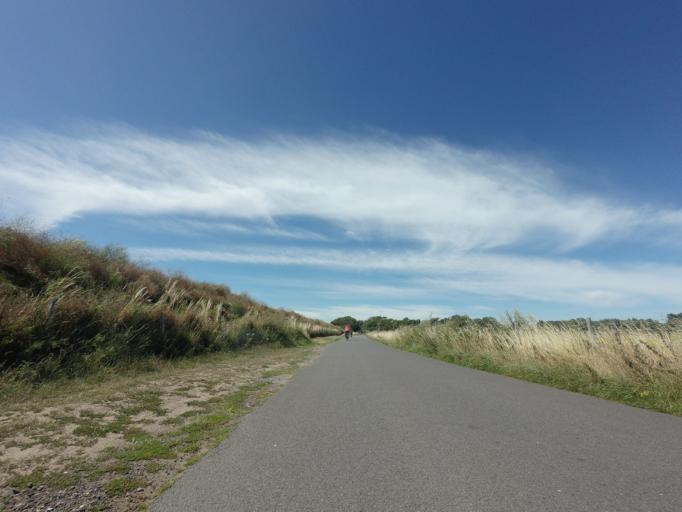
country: GB
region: England
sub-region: Kent
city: Deal
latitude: 51.2637
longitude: 1.3852
